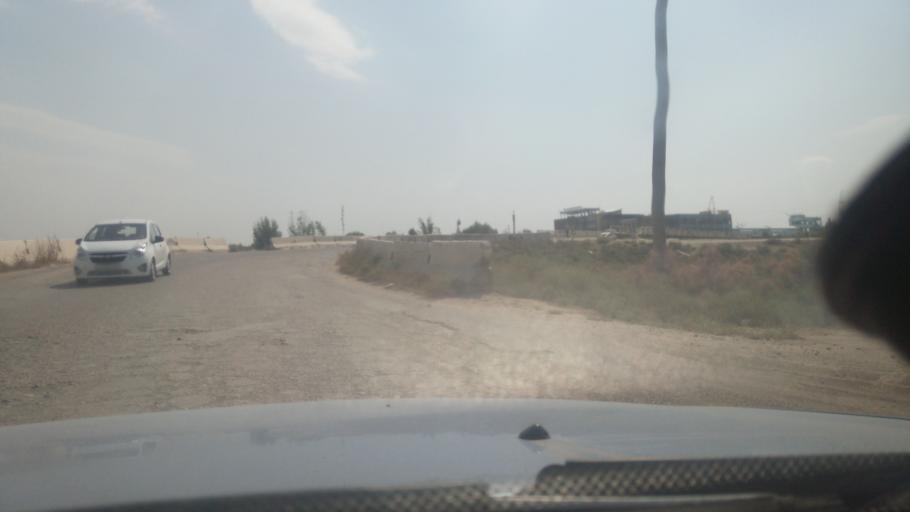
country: UZ
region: Sirdaryo
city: Guliston
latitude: 40.5229
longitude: 68.7690
